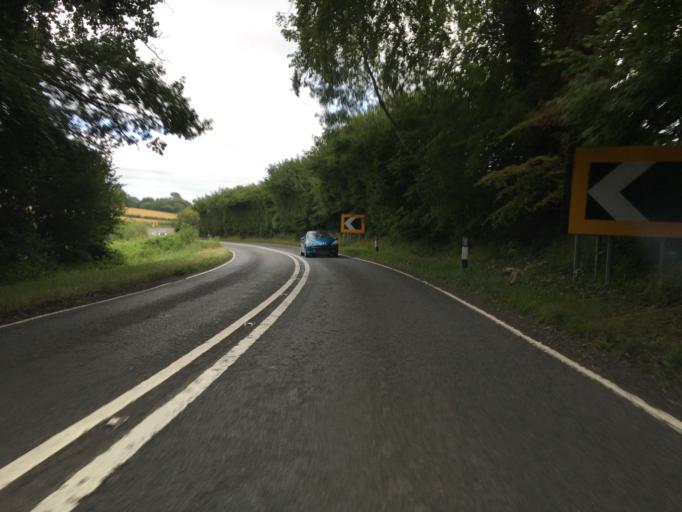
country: GB
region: England
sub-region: Hampshire
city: Four Marks
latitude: 51.0201
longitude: -1.0236
